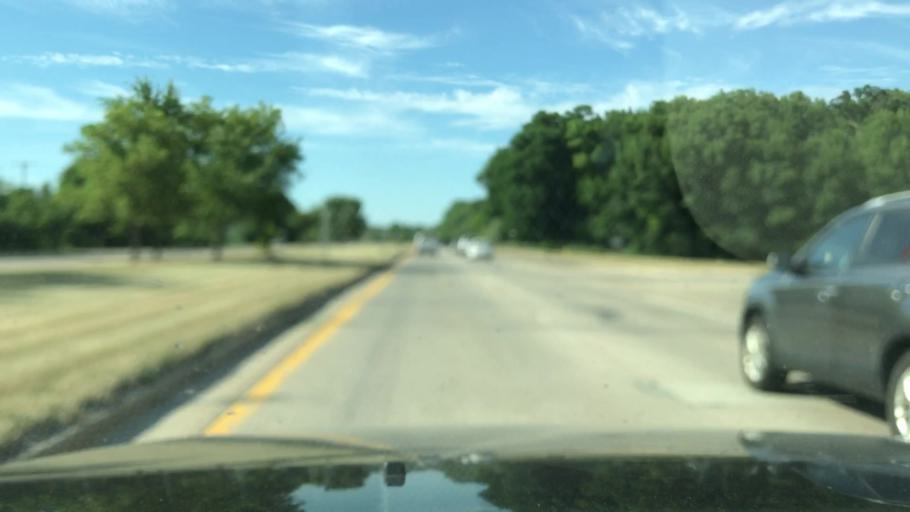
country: US
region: Michigan
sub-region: Kent County
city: East Grand Rapids
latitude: 42.9399
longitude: -85.5850
